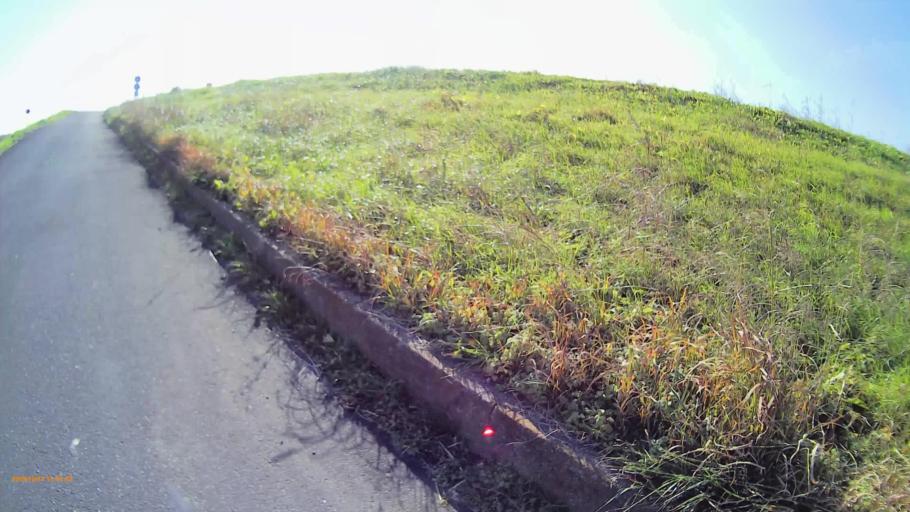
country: JP
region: Saitama
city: Kumagaya
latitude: 36.1241
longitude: 139.4035
